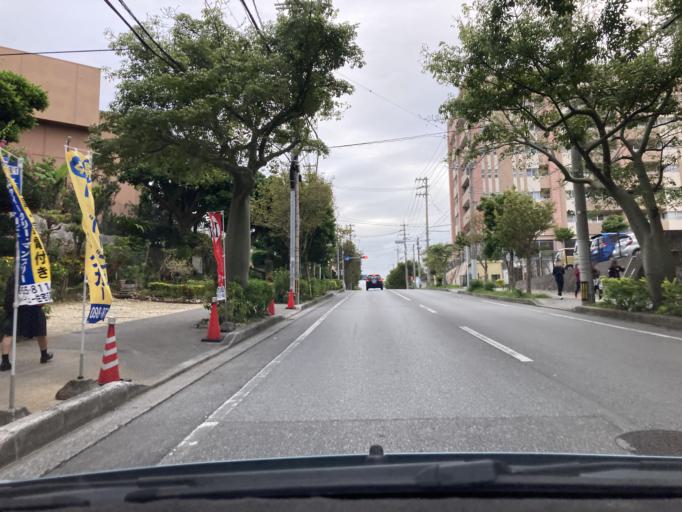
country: JP
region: Okinawa
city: Naha-shi
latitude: 26.2079
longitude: 127.6809
